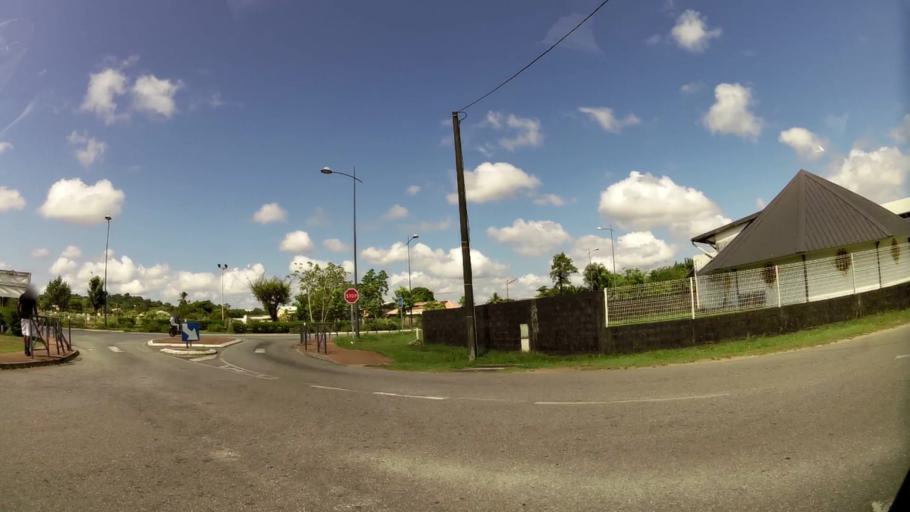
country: GF
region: Guyane
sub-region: Guyane
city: Cayenne
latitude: 4.9188
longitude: -52.3154
